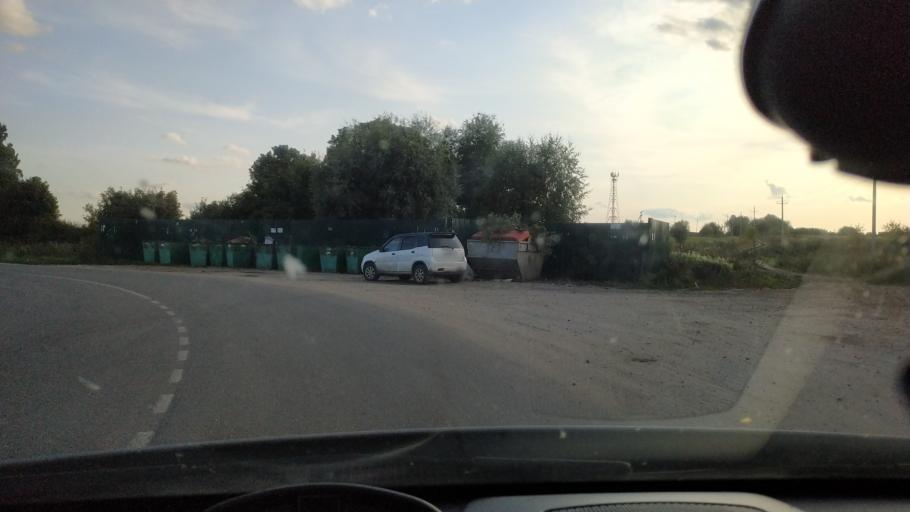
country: RU
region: Rjazan
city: Rybnoye
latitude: 54.8646
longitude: 39.6485
